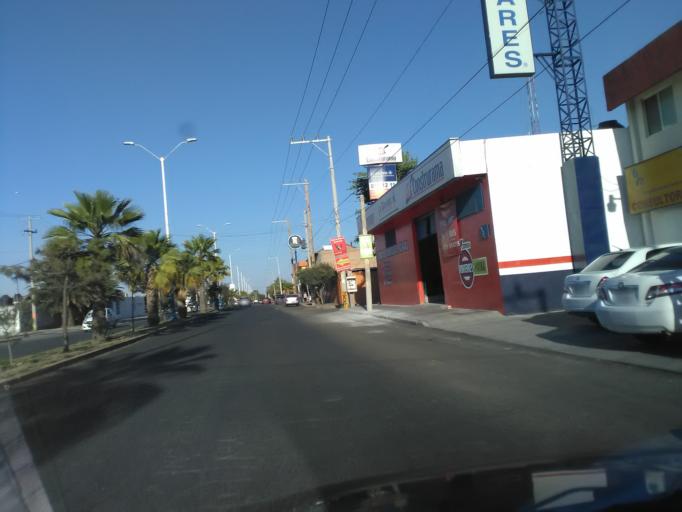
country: MX
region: Durango
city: Victoria de Durango
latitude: 24.0090
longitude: -104.6384
